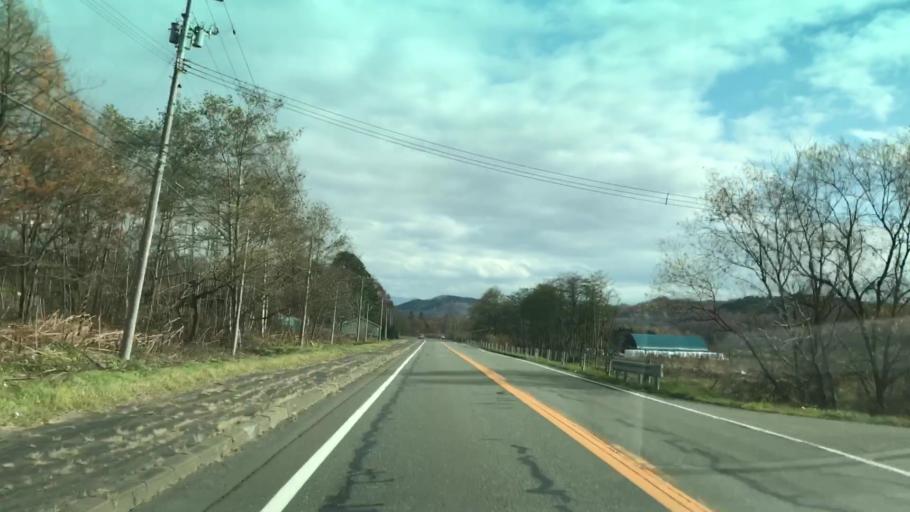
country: JP
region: Hokkaido
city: Shizunai-furukawacho
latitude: 42.7216
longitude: 142.2751
